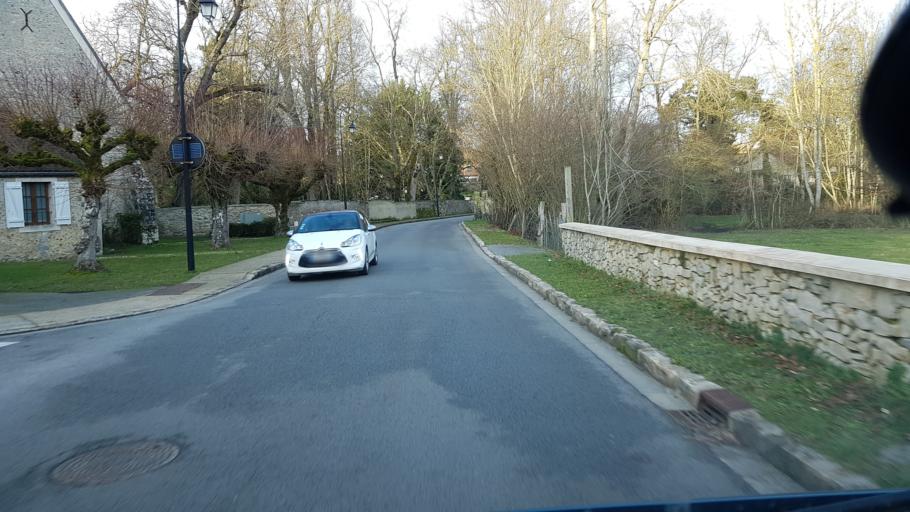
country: FR
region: Ile-de-France
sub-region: Departement des Yvelines
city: Saint-Leger-en-Yvelines
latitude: 48.6789
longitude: 1.7543
